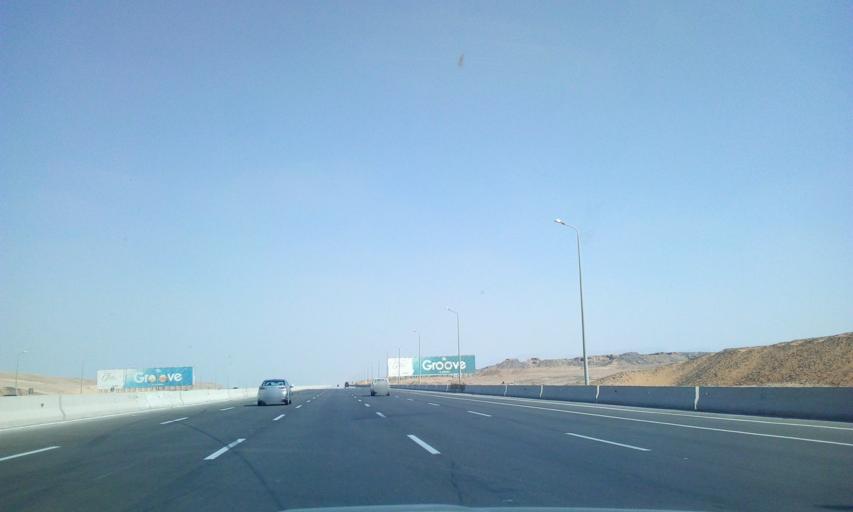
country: EG
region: As Suways
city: Ain Sukhna
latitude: 29.7085
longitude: 32.0828
